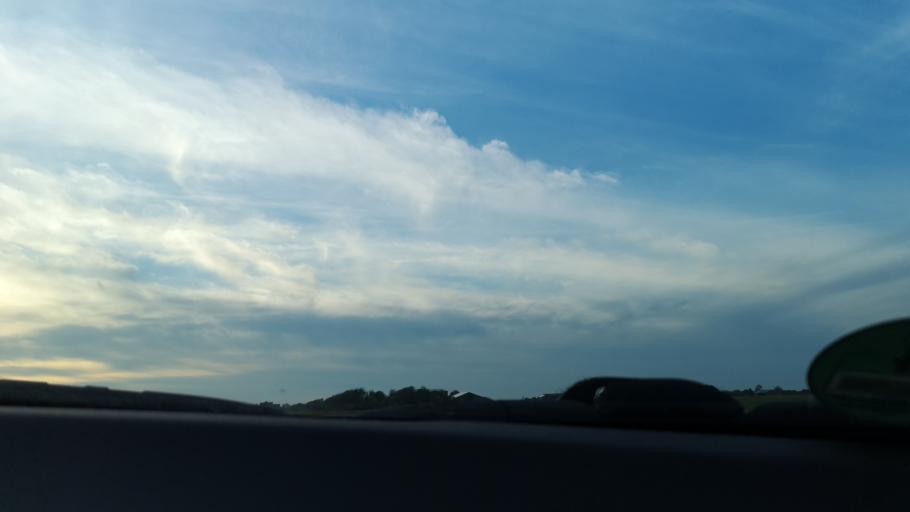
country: DE
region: Schleswig-Holstein
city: Pellworm
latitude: 54.5153
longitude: 8.6247
